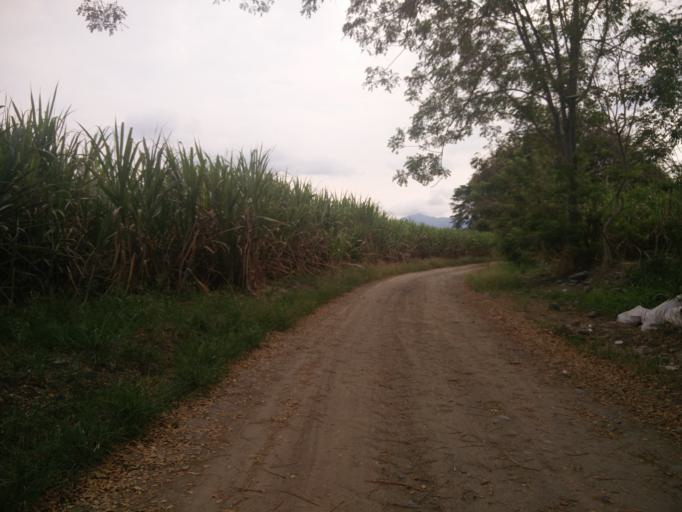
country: CO
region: Valle del Cauca
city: Buga
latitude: 3.8901
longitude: -76.3223
